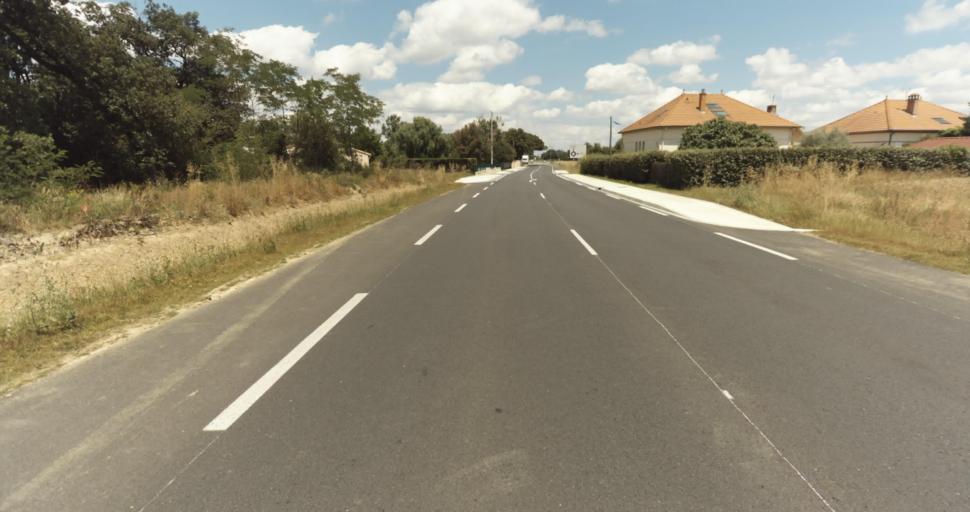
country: FR
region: Midi-Pyrenees
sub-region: Departement de la Haute-Garonne
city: Fontenilles
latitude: 43.5374
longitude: 1.1867
